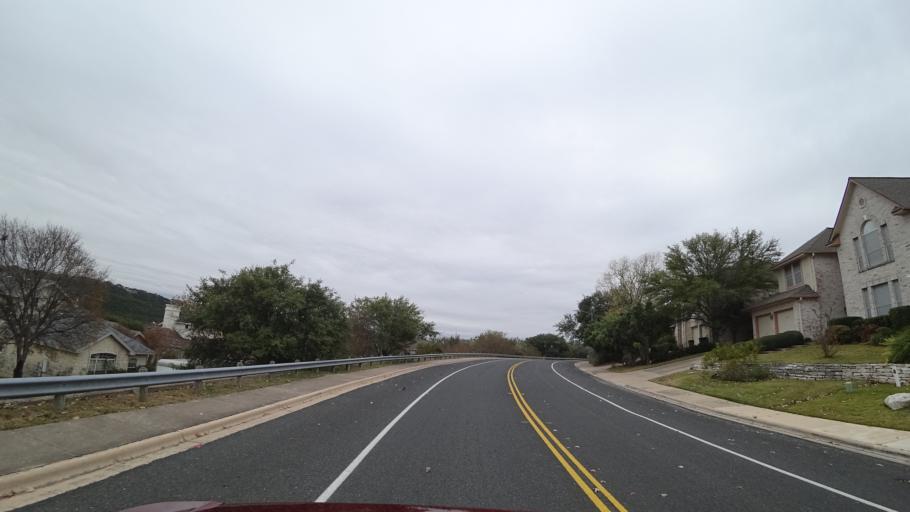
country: US
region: Texas
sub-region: Williamson County
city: Jollyville
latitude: 30.3808
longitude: -97.7866
